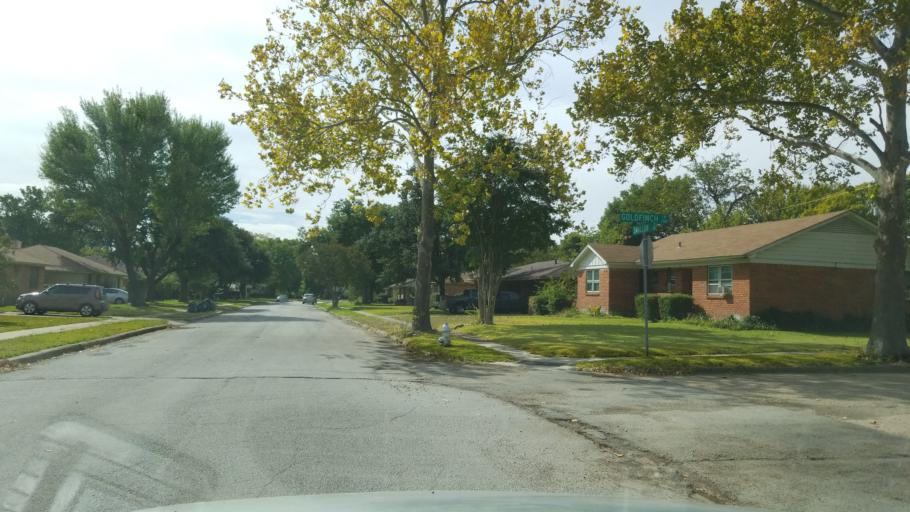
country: US
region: Texas
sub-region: Dallas County
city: Garland
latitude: 32.9019
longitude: -96.6609
